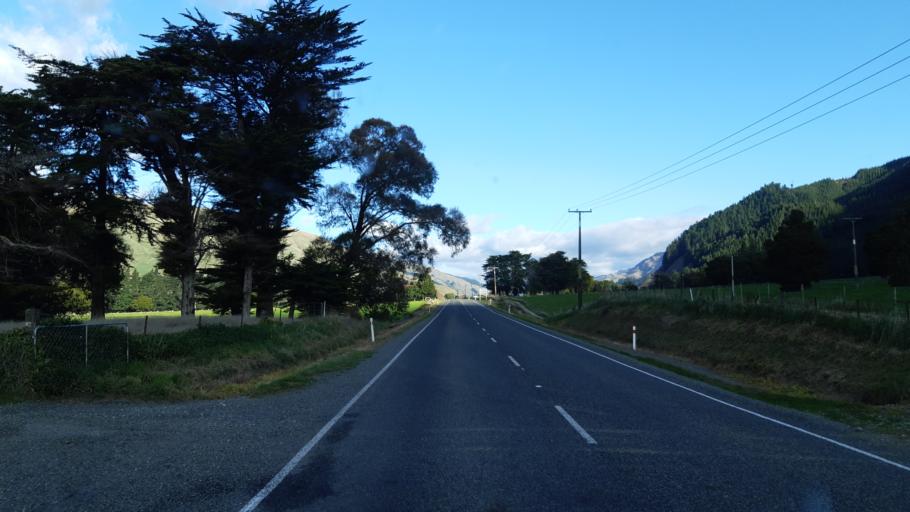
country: NZ
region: Marlborough
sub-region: Marlborough District
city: Picton
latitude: -41.2970
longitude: 173.7702
